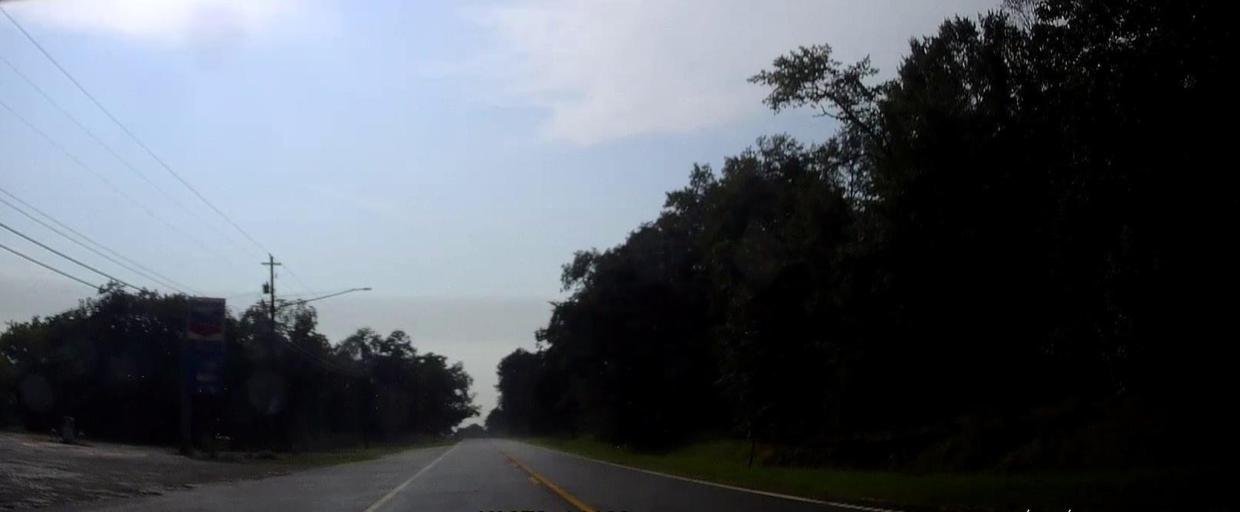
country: US
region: Georgia
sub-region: Twiggs County
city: Jeffersonville
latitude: 32.6034
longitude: -83.2488
